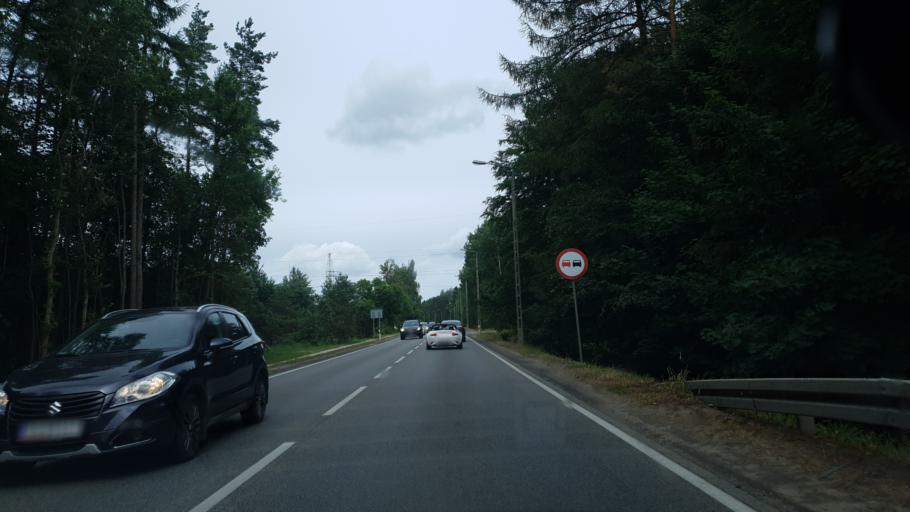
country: PL
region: Pomeranian Voivodeship
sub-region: Powiat kartuski
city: Chwaszczyno
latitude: 54.4319
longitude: 18.3940
